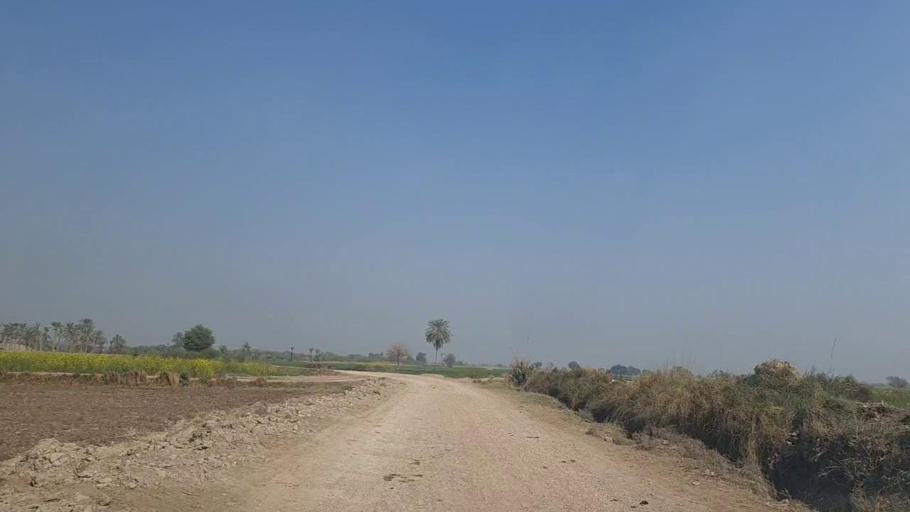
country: PK
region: Sindh
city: Nawabshah
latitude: 26.2324
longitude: 68.4936
